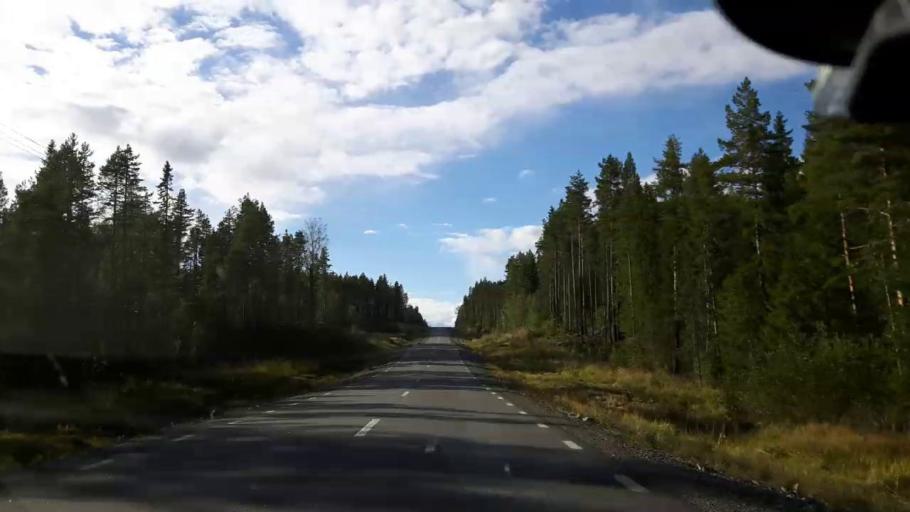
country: SE
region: Jaemtland
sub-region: Stroemsunds Kommun
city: Stroemsund
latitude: 63.5618
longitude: 15.8029
